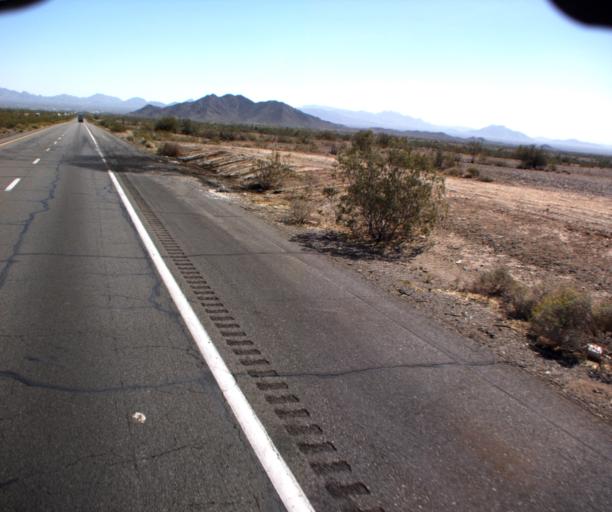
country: US
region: Arizona
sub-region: La Paz County
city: Quartzsite
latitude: 33.6502
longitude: -114.3069
